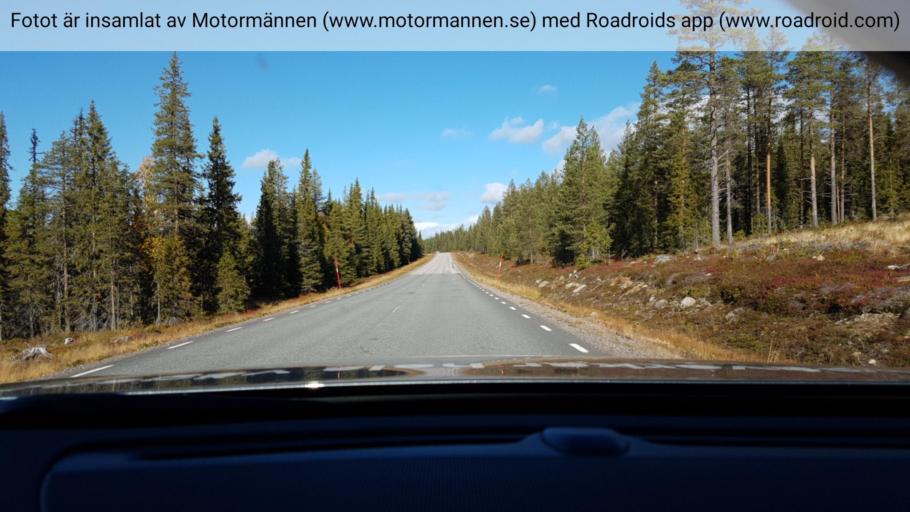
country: SE
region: Norrbotten
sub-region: Arjeplogs Kommun
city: Arjeplog
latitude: 65.8026
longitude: 18.4669
